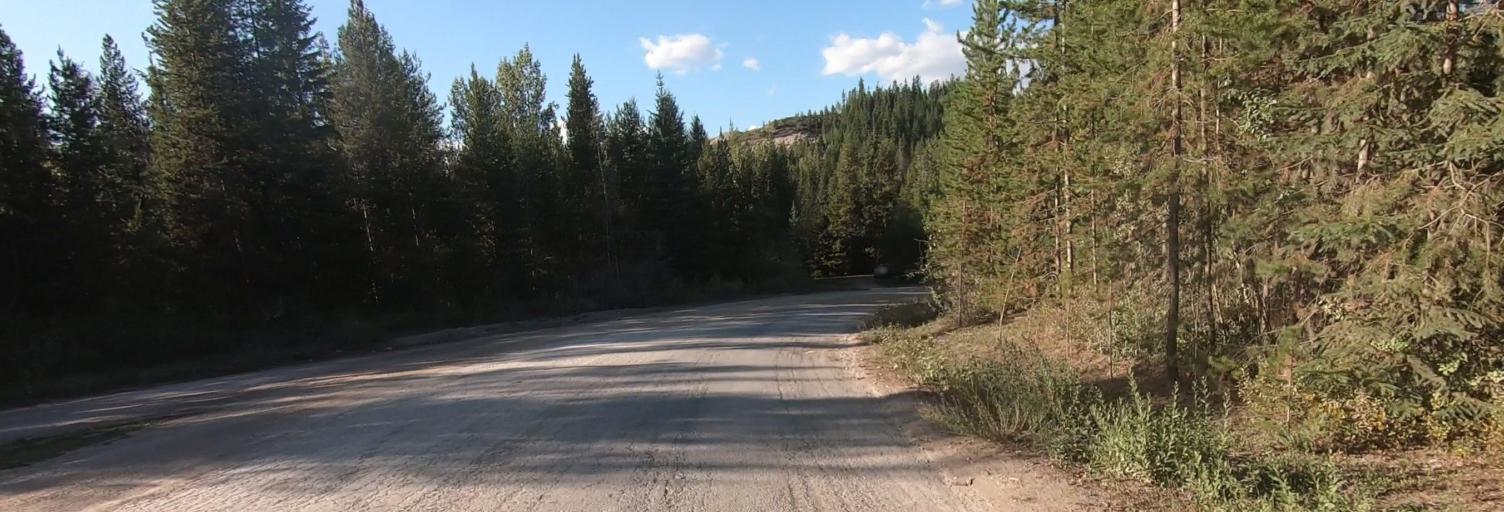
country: CA
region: British Columbia
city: Golden
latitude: 51.4974
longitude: -117.1761
